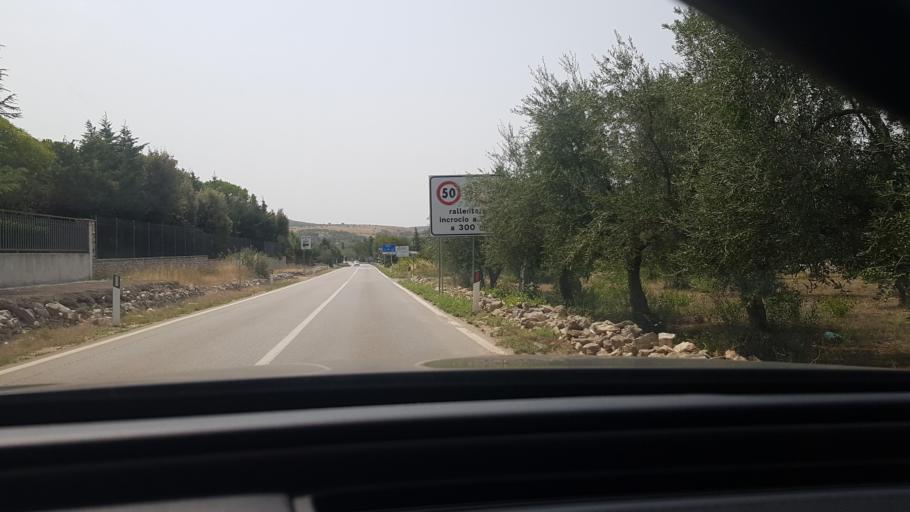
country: IT
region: Apulia
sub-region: Provincia di Barletta - Andria - Trani
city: Andria
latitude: 41.1200
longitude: 16.2847
